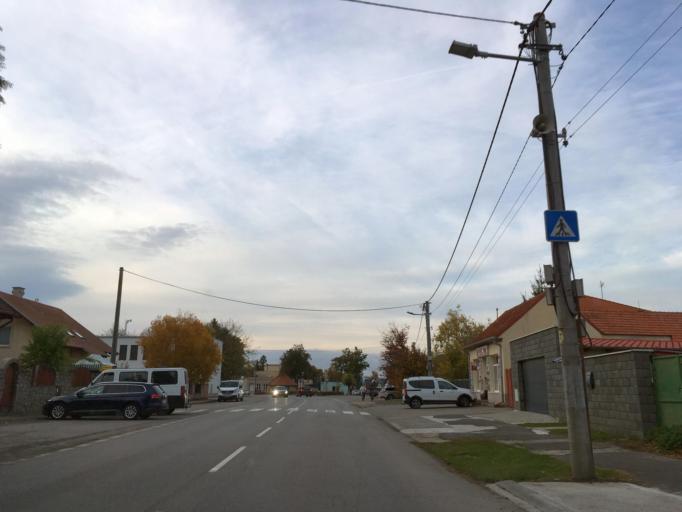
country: SK
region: Trnavsky
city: Samorin
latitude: 48.0984
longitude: 17.3554
